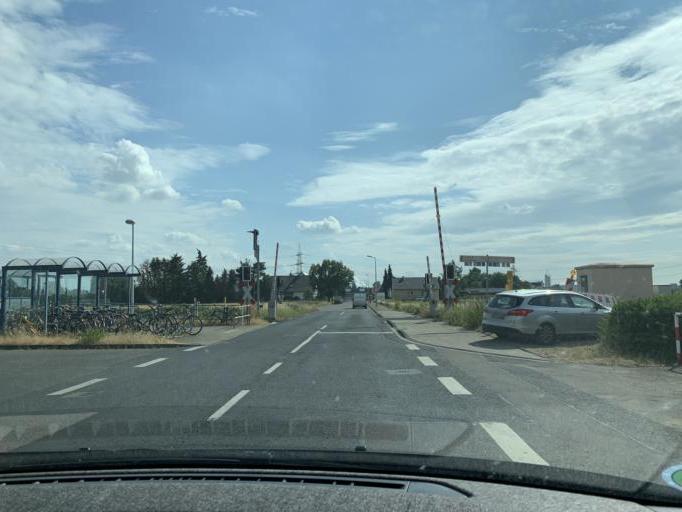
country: DE
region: North Rhine-Westphalia
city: Julich
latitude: 50.8990
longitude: 6.3920
